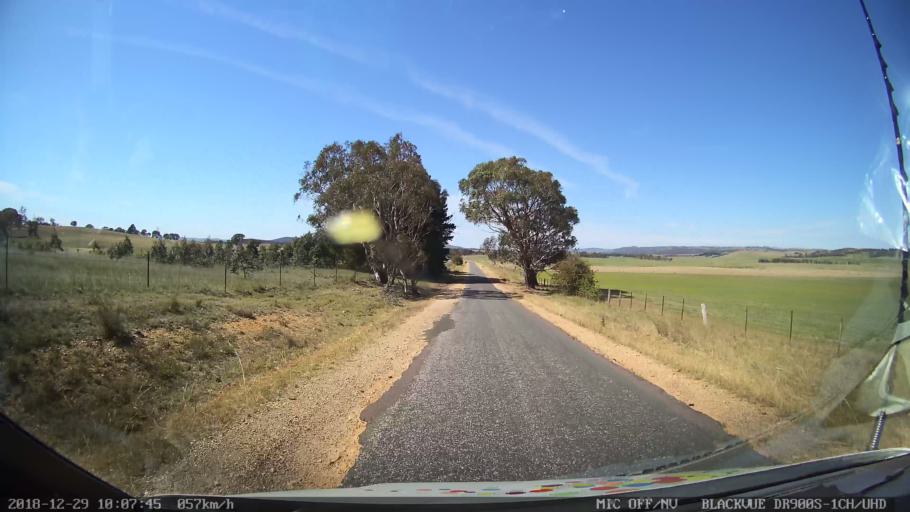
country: AU
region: New South Wales
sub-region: Yass Valley
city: Gundaroo
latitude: -34.8557
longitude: 149.4524
